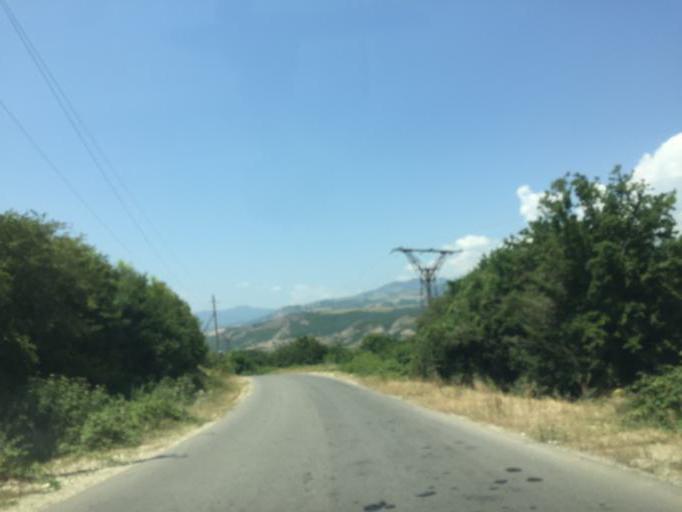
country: AZ
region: Tartar Rayon
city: Martakert
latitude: 40.1427
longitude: 46.5820
